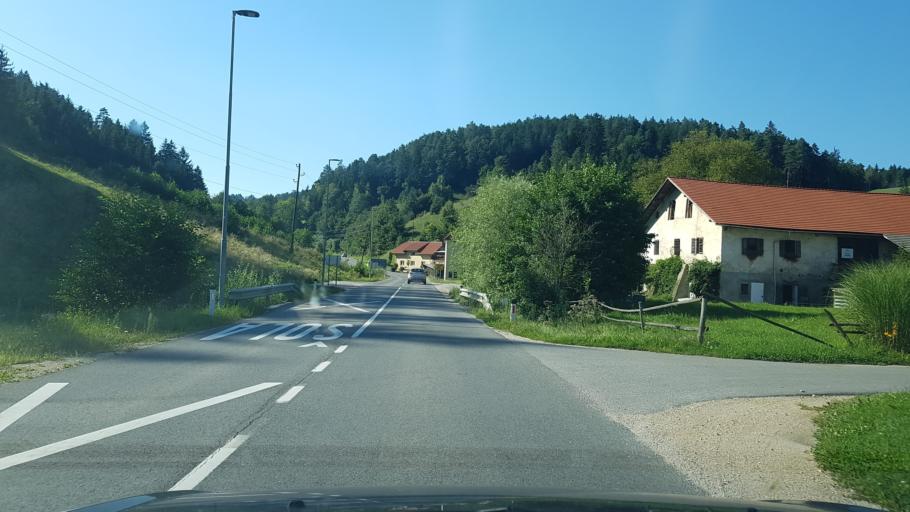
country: SI
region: Slovenj Gradec
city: Slovenj Gradec
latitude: 46.5177
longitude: 15.0418
